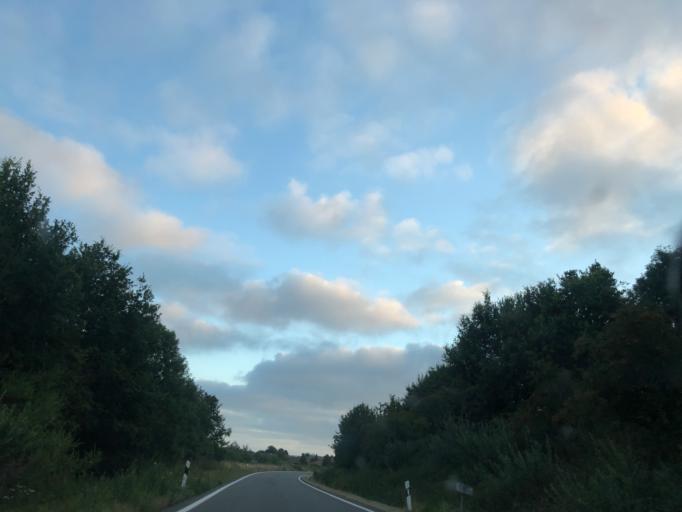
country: DE
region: Lower Saxony
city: Bunde
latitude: 53.1659
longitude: 7.2864
